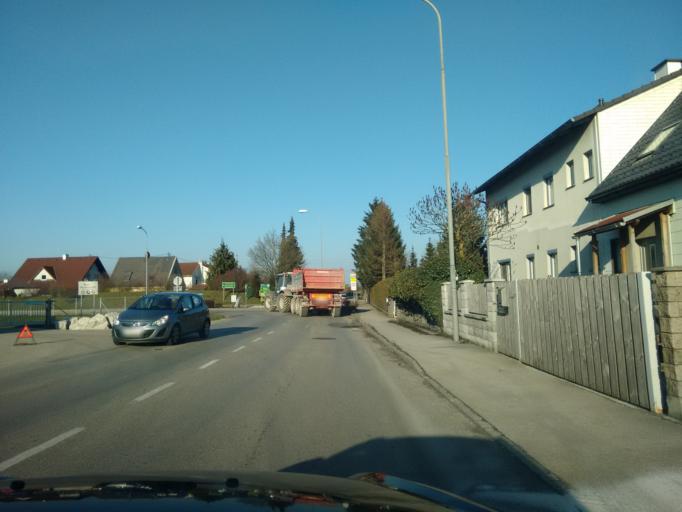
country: AT
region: Upper Austria
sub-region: Wels-Land
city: Marchtrenk
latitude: 48.1933
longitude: 14.0920
